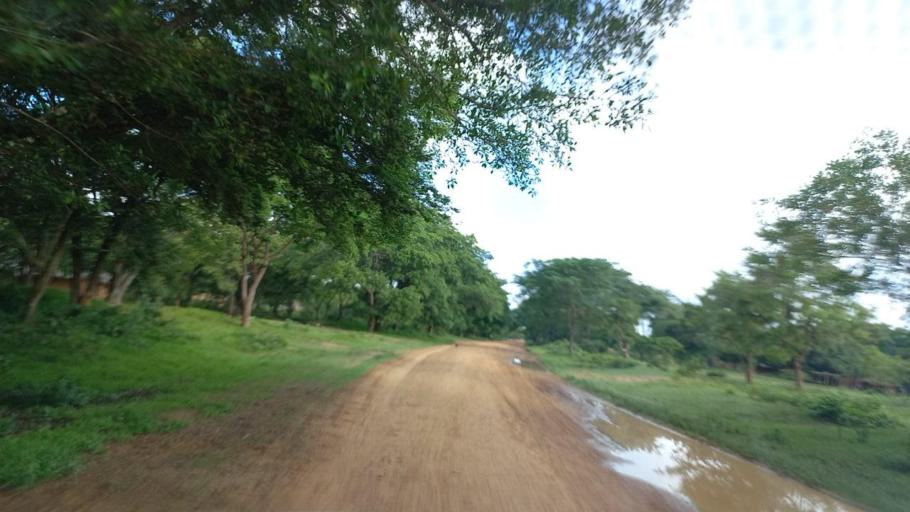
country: ZM
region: North-Western
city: Kabompo
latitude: -13.3741
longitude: 24.2982
